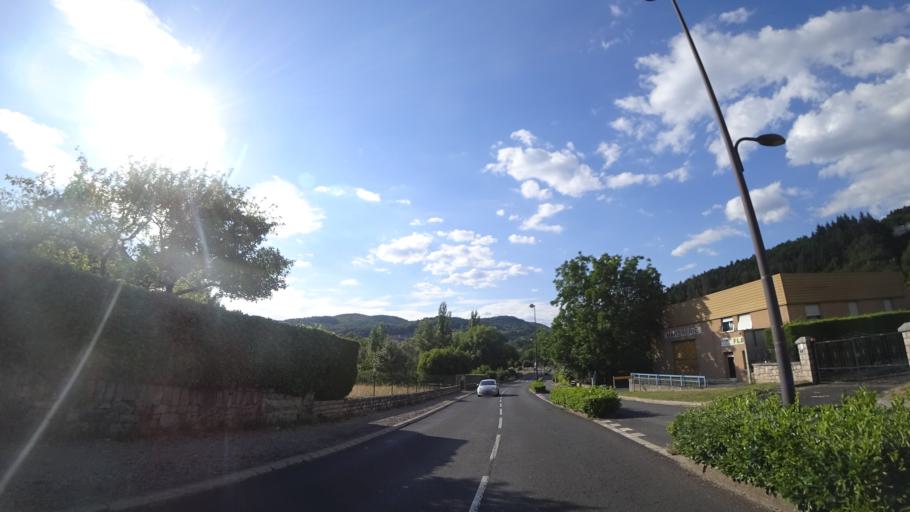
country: FR
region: Languedoc-Roussillon
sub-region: Departement de la Lozere
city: La Canourgue
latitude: 44.4376
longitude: 3.1996
